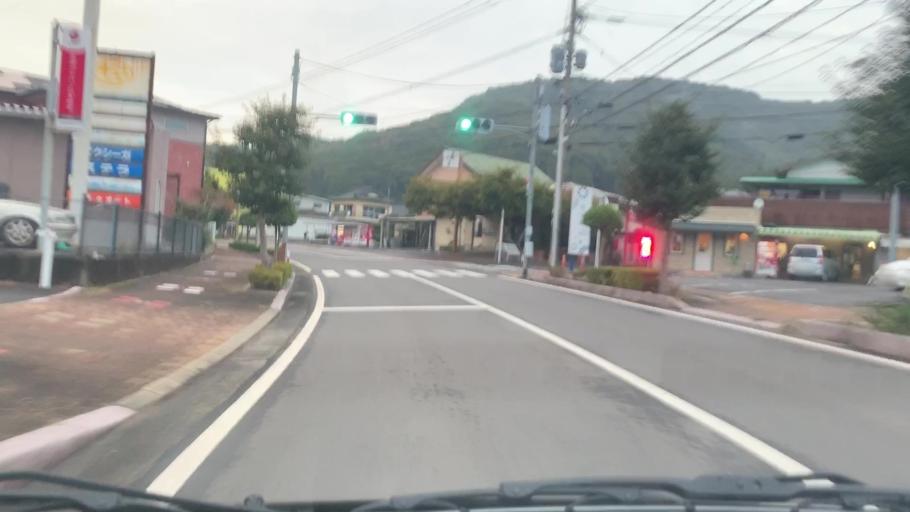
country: JP
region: Saga Prefecture
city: Ureshinomachi-shimojuku
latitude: 33.1496
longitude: 129.9008
